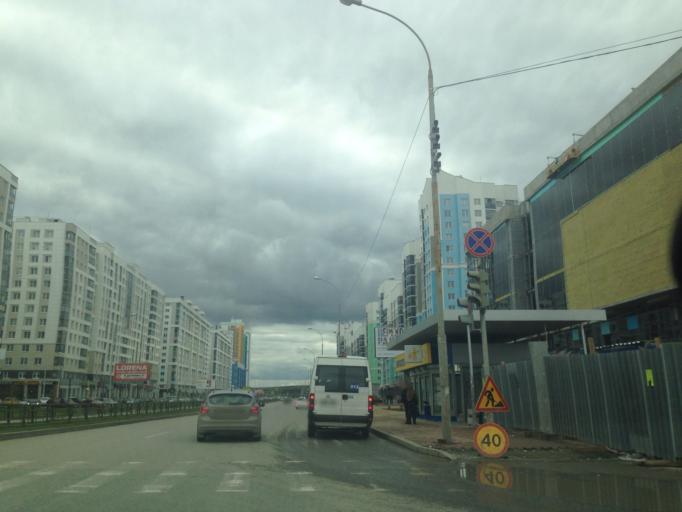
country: RU
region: Sverdlovsk
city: Shirokaya Rechka
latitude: 56.7931
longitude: 60.5213
